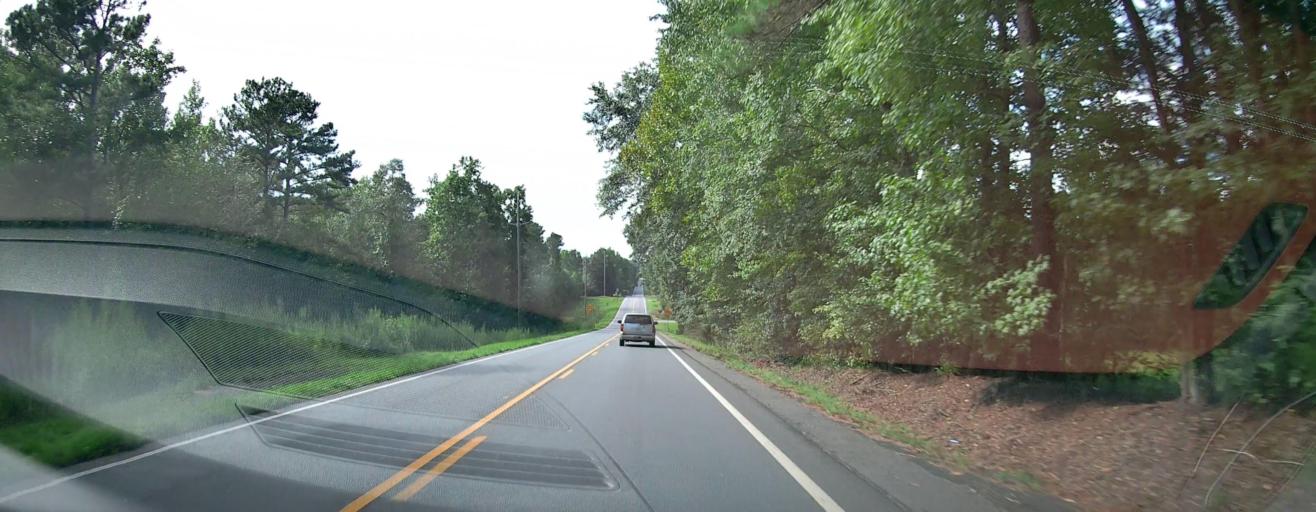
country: US
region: Georgia
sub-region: Upson County
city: Hannahs Mill
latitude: 32.9794
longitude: -84.4969
